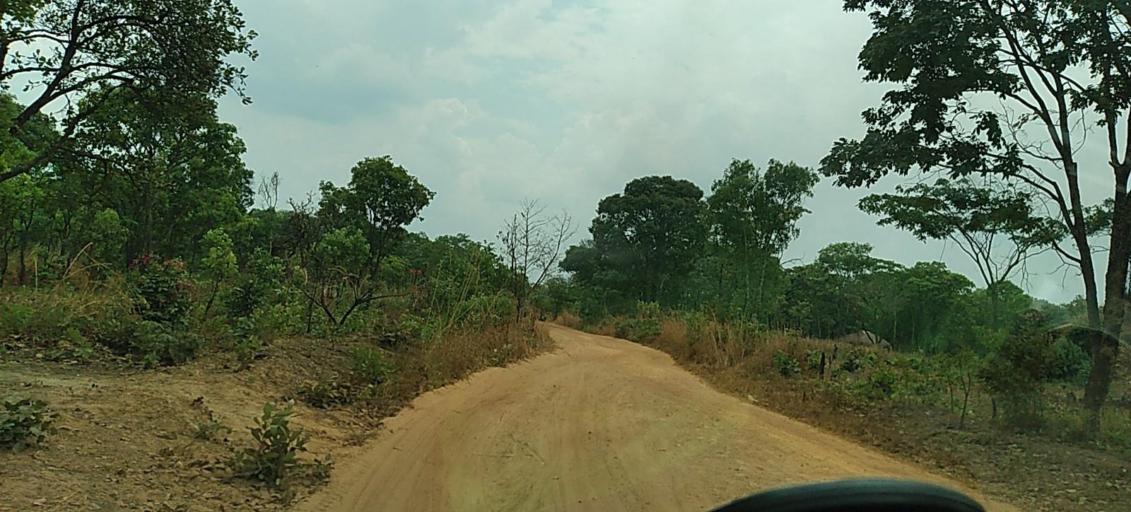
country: ZM
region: North-Western
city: Kansanshi
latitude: -12.0387
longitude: 26.3241
